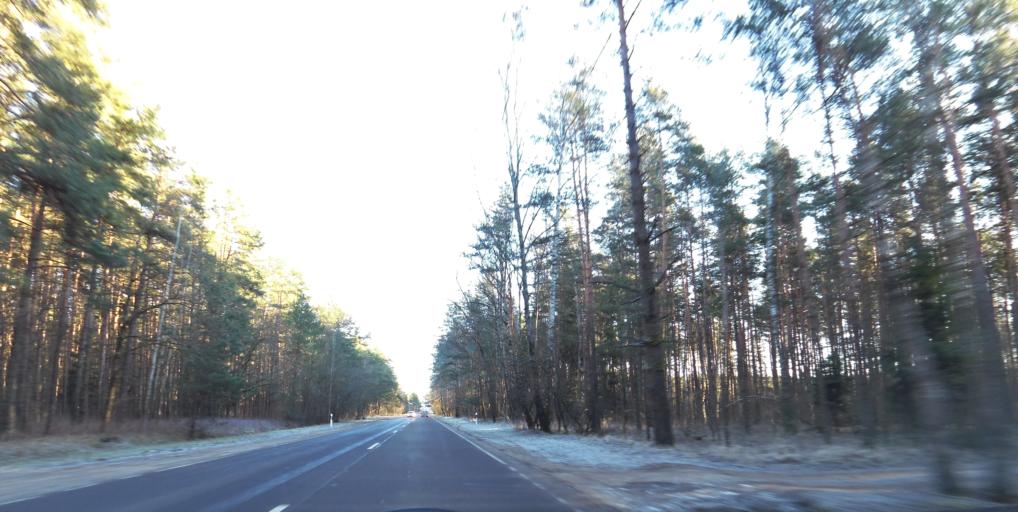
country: LT
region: Vilnius County
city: Lazdynai
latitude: 54.6428
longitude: 25.1684
